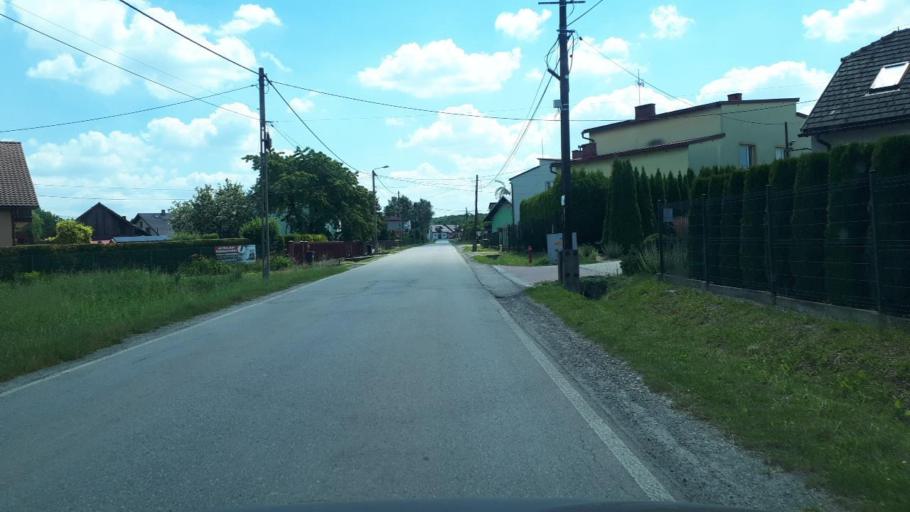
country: PL
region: Lesser Poland Voivodeship
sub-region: Powiat oswiecimski
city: Brzeszcze
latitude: 49.9510
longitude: 19.1442
